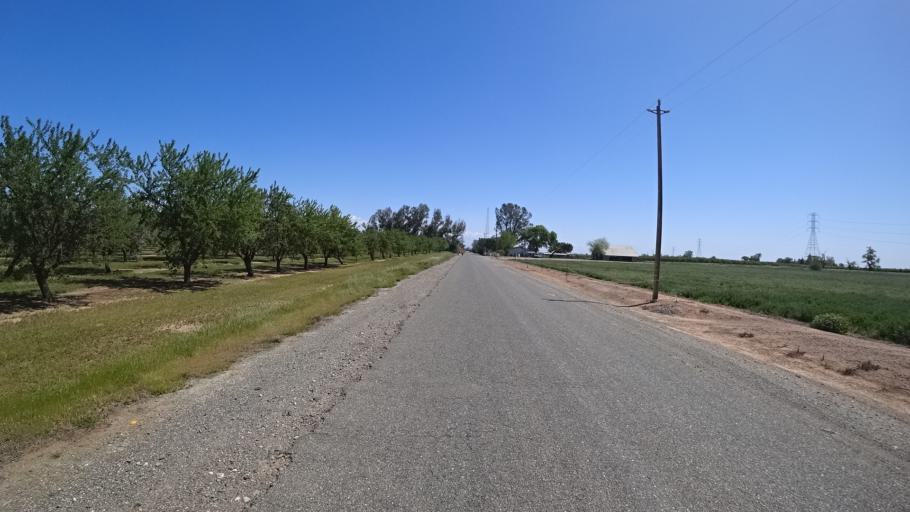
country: US
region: California
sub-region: Glenn County
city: Orland
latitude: 39.7977
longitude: -122.1762
